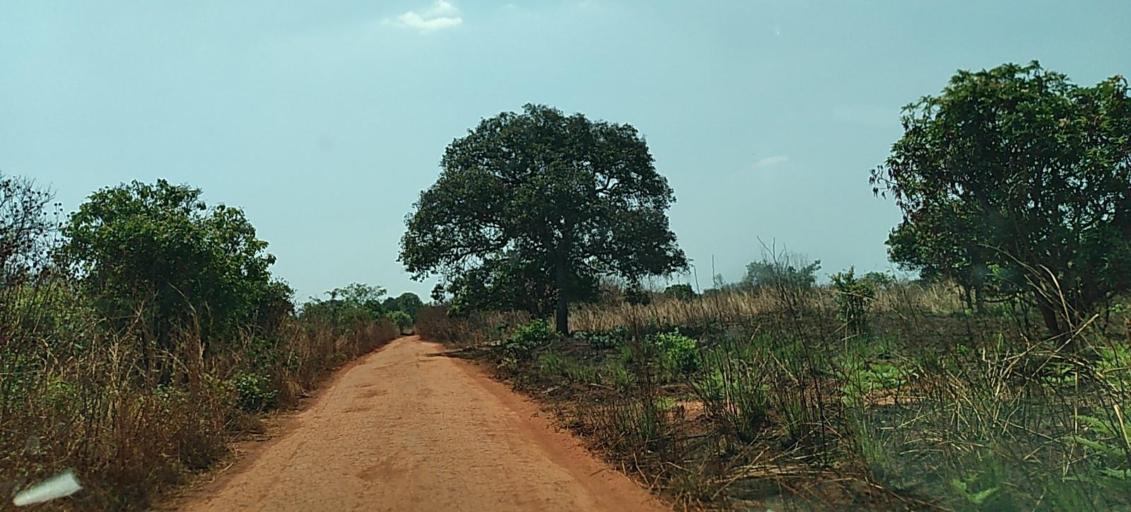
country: ZM
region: North-Western
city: Solwezi
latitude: -12.1326
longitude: 26.3157
